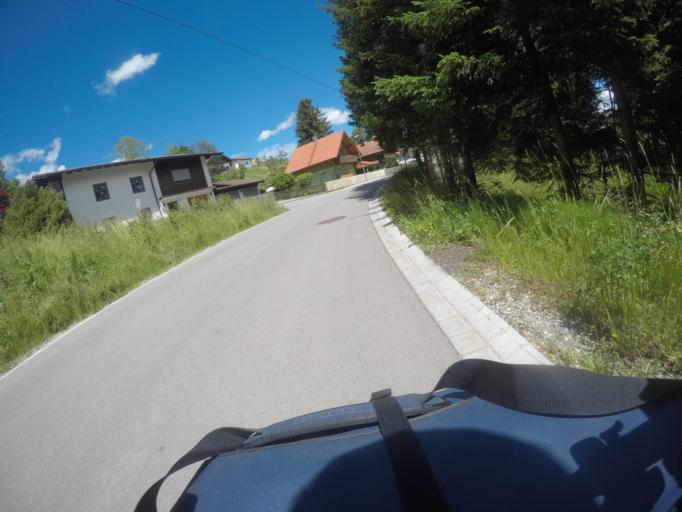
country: DE
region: Bavaria
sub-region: Upper Bavaria
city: Prem
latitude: 47.6906
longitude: 10.7954
